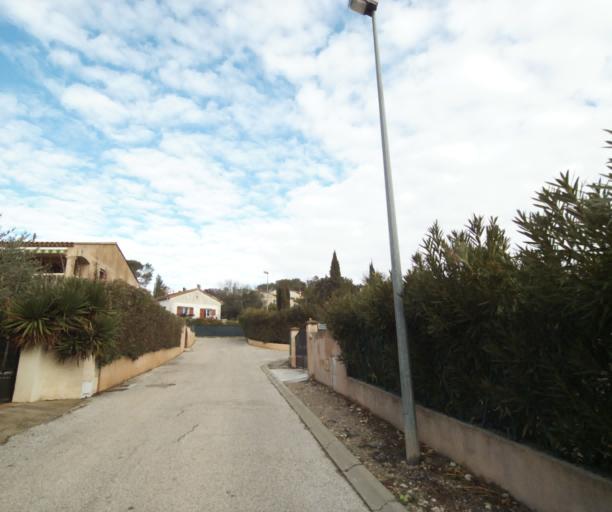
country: FR
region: Provence-Alpes-Cote d'Azur
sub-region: Departement du Var
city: Trans-en-Provence
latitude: 43.5006
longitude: 6.4811
